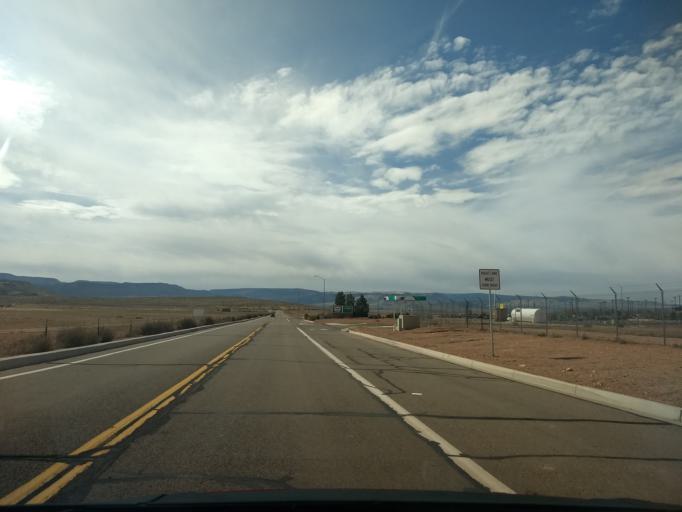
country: US
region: Utah
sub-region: Washington County
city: Washington
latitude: 37.0324
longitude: -113.5043
